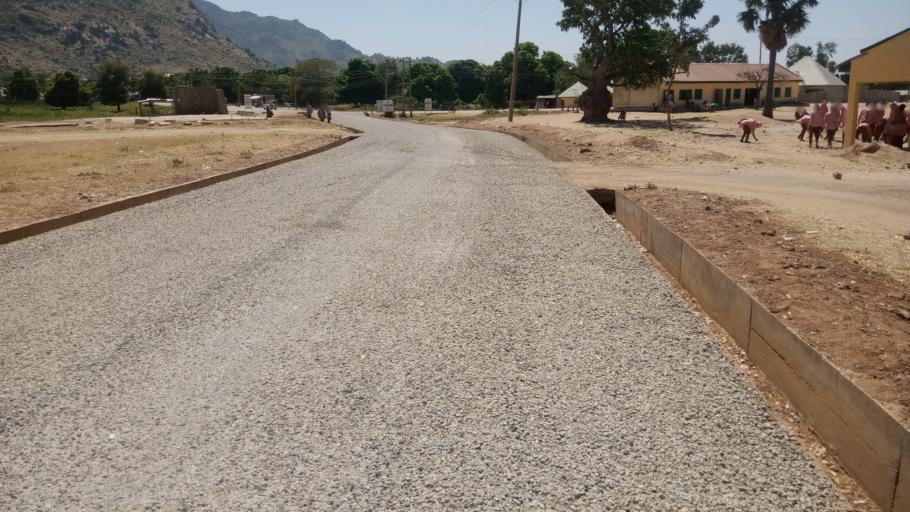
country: NG
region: Adamawa
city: Little Gombi
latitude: 10.2404
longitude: 12.9347
